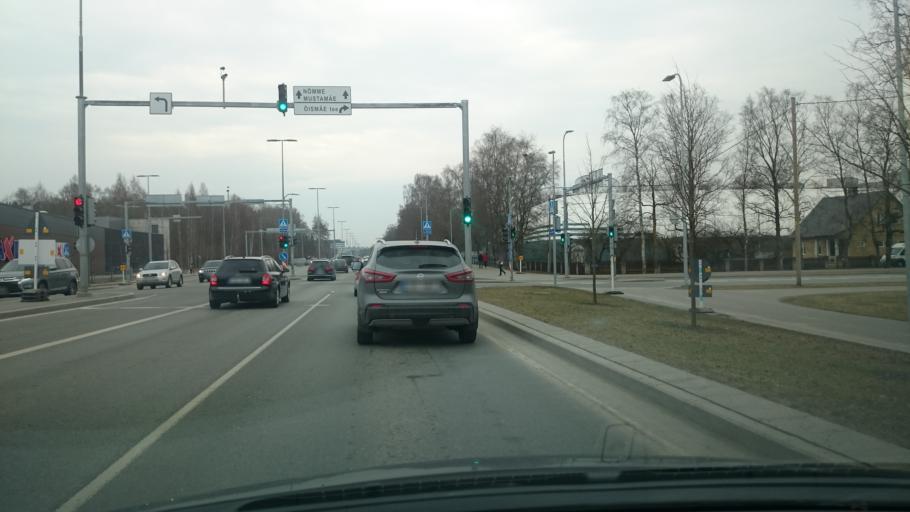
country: EE
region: Harju
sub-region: Saue vald
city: Laagri
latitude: 59.4213
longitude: 24.6492
